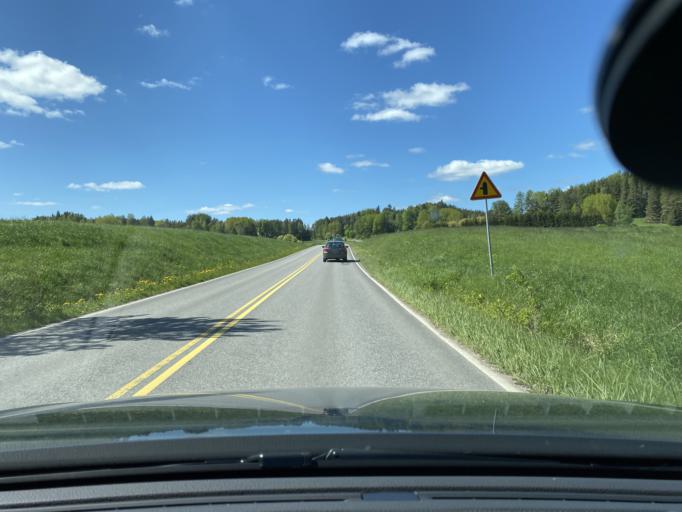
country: FI
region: Varsinais-Suomi
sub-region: Salo
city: Halikko
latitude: 60.3660
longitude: 23.0013
